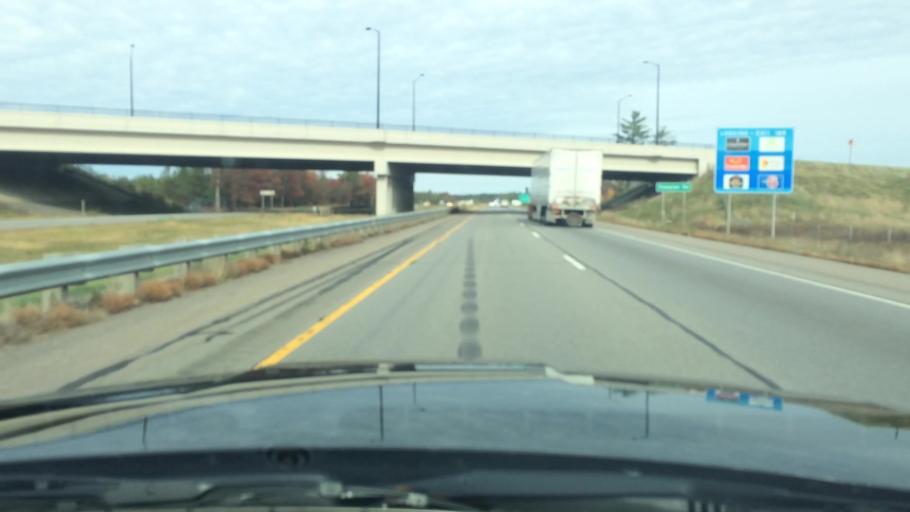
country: US
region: Wisconsin
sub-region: Marathon County
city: Evergreen
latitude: 44.8432
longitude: -89.6464
